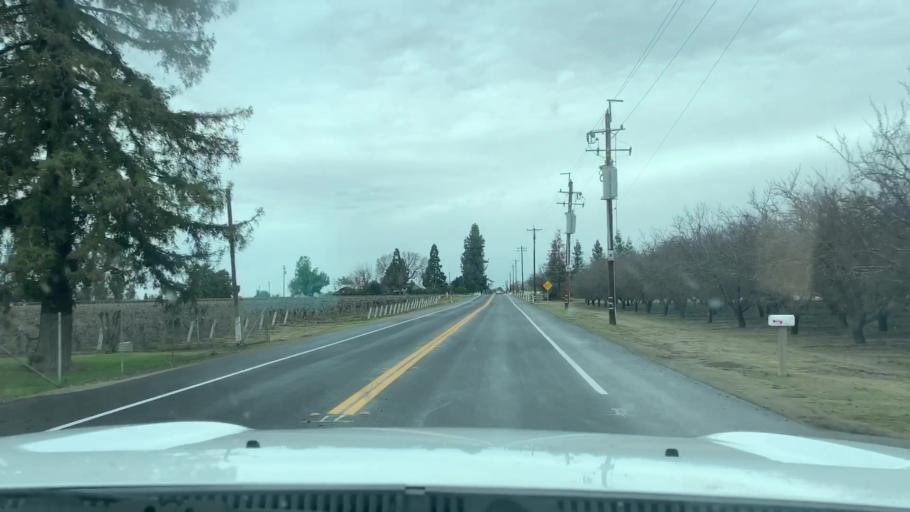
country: US
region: California
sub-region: Fresno County
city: Fowler
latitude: 36.5690
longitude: -119.6825
